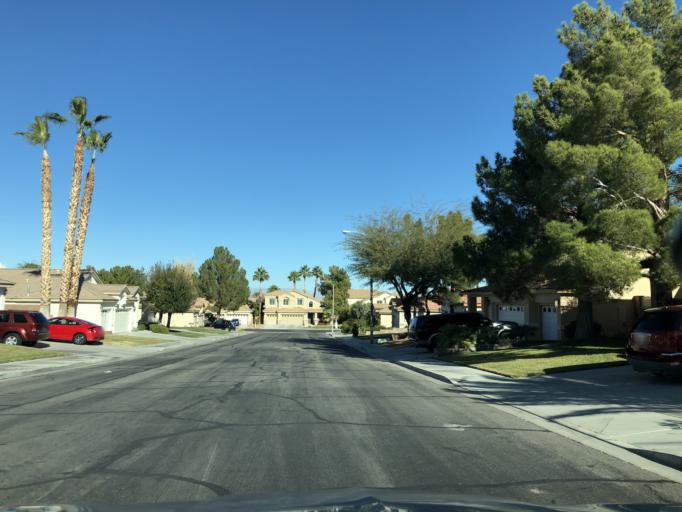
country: US
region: Nevada
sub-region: Clark County
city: Whitney
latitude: 36.0118
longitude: -115.0839
